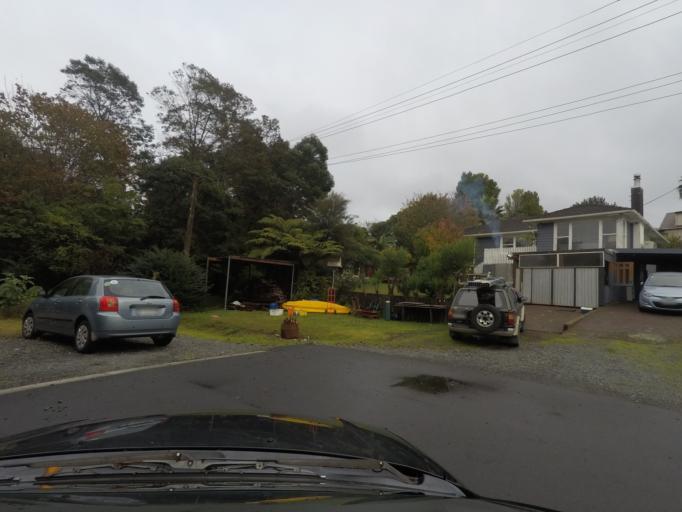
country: NZ
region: Auckland
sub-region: Auckland
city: Rosebank
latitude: -36.7605
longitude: 174.5957
